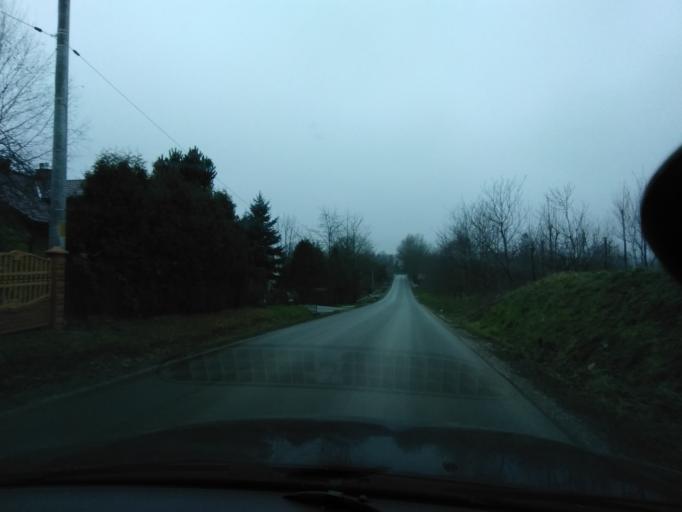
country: PL
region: Subcarpathian Voivodeship
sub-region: Powiat przeworski
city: Zurawiczki
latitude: 50.0036
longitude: 22.4831
